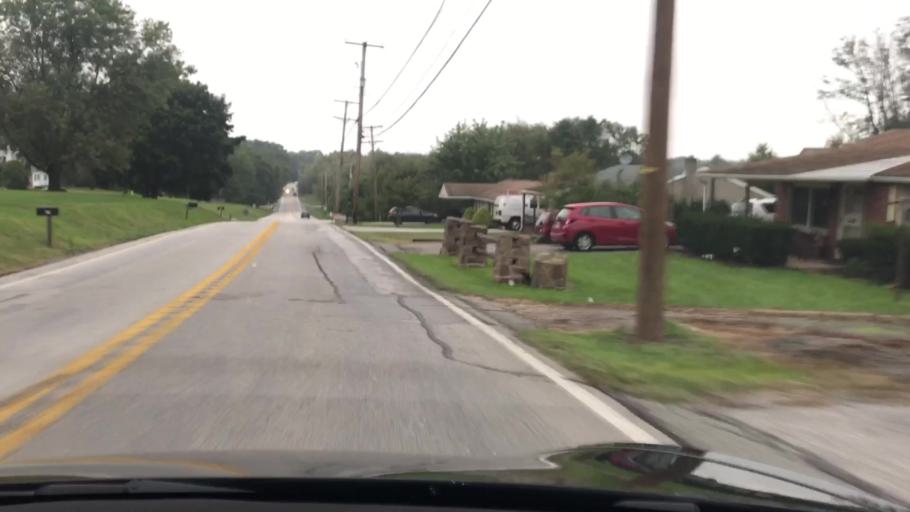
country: US
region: Pennsylvania
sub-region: York County
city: Shiloh
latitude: 40.0319
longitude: -76.7888
